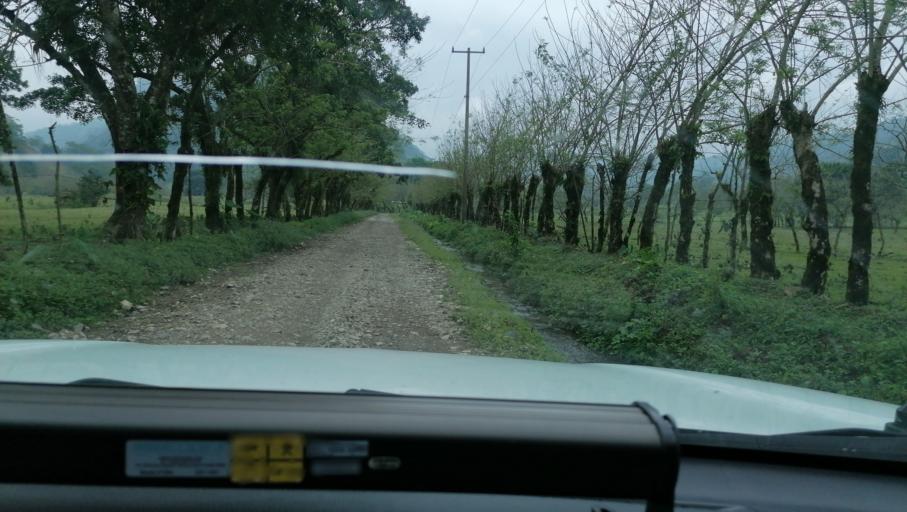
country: MX
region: Chiapas
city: Ixtacomitan
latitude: 17.3638
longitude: -93.1739
